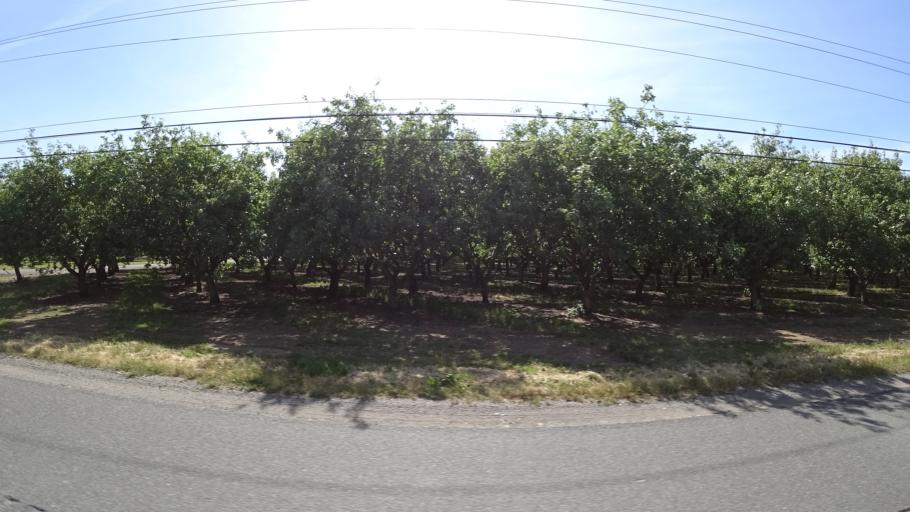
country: US
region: California
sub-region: Tehama County
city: Gerber
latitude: 40.1211
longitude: -122.1198
